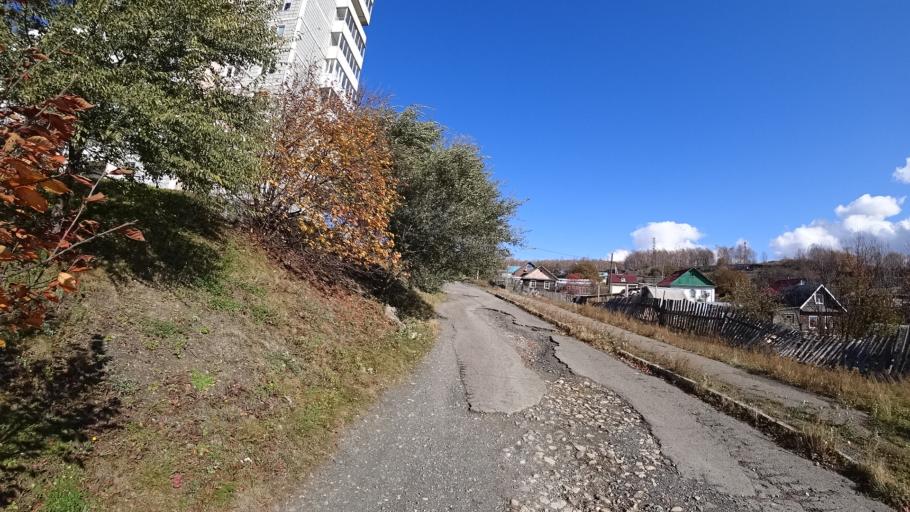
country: RU
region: Khabarovsk Krai
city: Amursk
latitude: 50.2396
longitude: 136.9181
